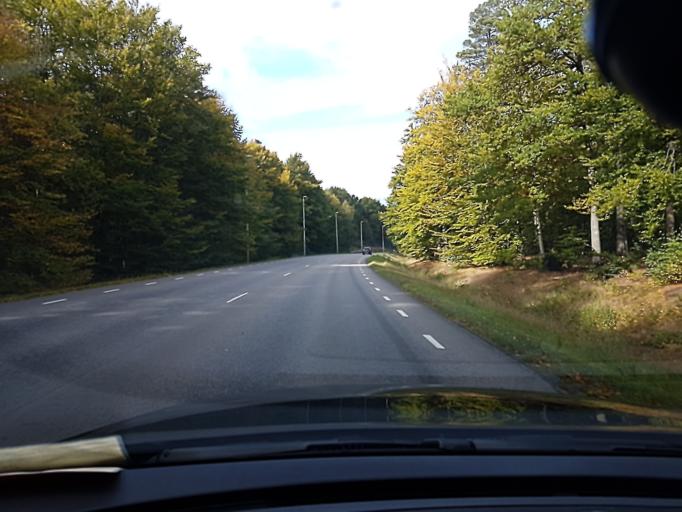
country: SE
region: Kronoberg
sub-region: Vaxjo Kommun
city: Vaexjoe
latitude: 56.8659
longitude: 14.7904
